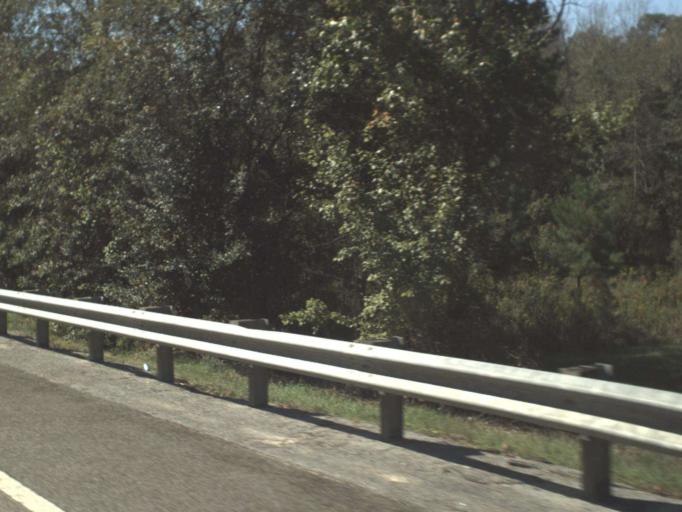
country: US
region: Alabama
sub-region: Geneva County
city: Samson
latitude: 30.9743
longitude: -86.1352
